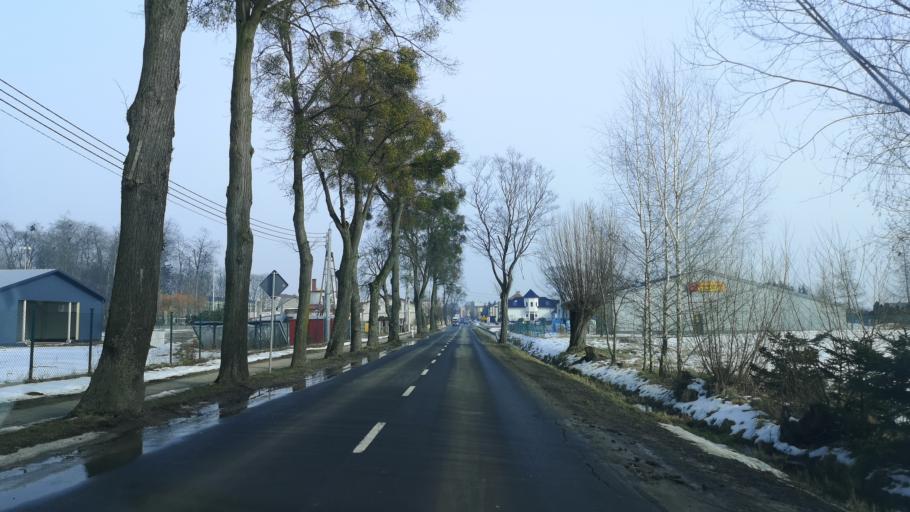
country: PL
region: Warmian-Masurian Voivodeship
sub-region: Powiat nowomiejski
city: Biskupiec
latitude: 53.4995
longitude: 19.3395
